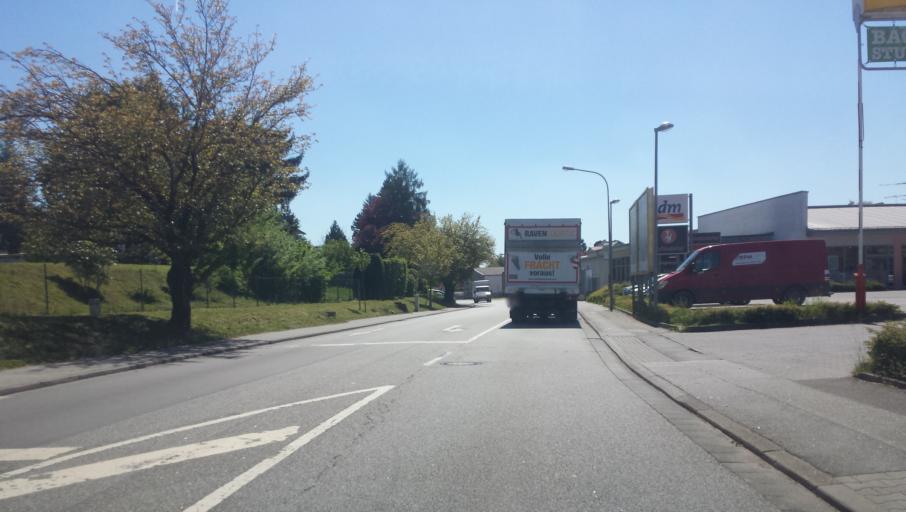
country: DE
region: Hesse
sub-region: Regierungsbezirk Darmstadt
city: Furth
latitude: 49.6567
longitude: 8.7875
